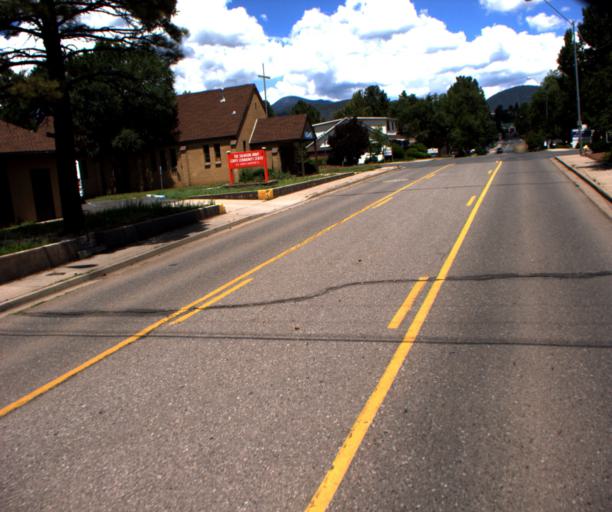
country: US
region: Arizona
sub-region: Coconino County
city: Flagstaff
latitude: 35.2033
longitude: -111.6490
